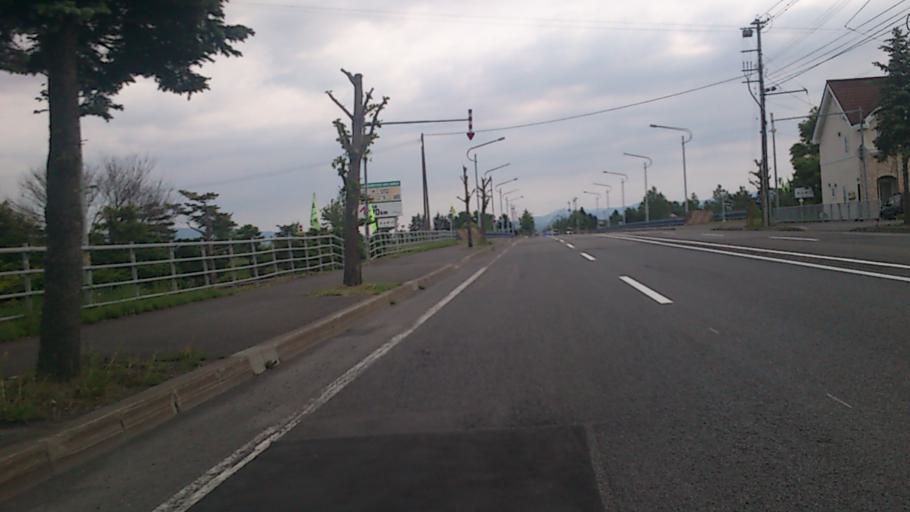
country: JP
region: Hokkaido
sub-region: Asahikawa-shi
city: Asahikawa
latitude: 43.8203
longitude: 142.4493
